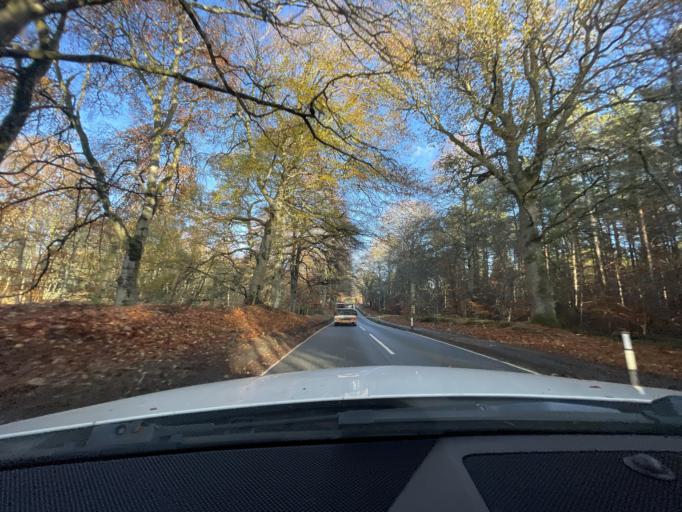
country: GB
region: Scotland
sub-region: Highland
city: Inverness
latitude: 57.4336
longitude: -4.2736
